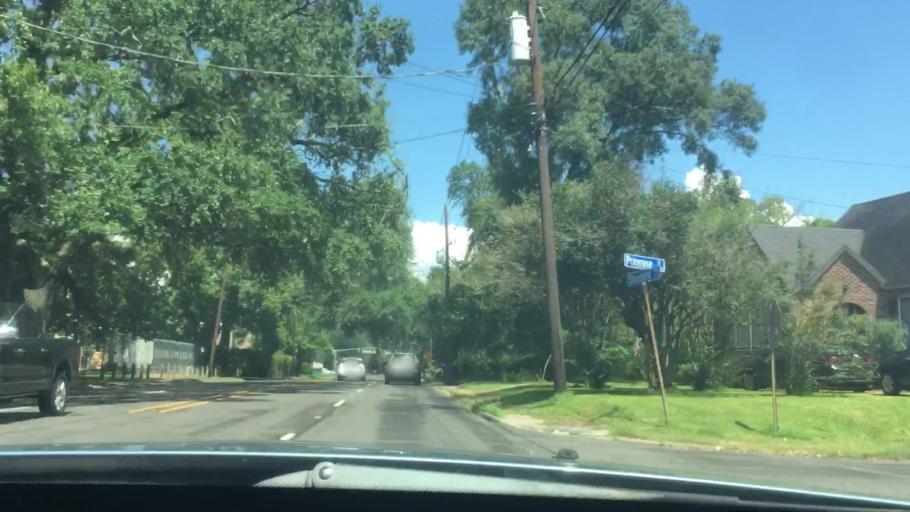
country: US
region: Louisiana
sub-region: East Baton Rouge Parish
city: Baton Rouge
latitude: 30.4143
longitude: -91.1578
